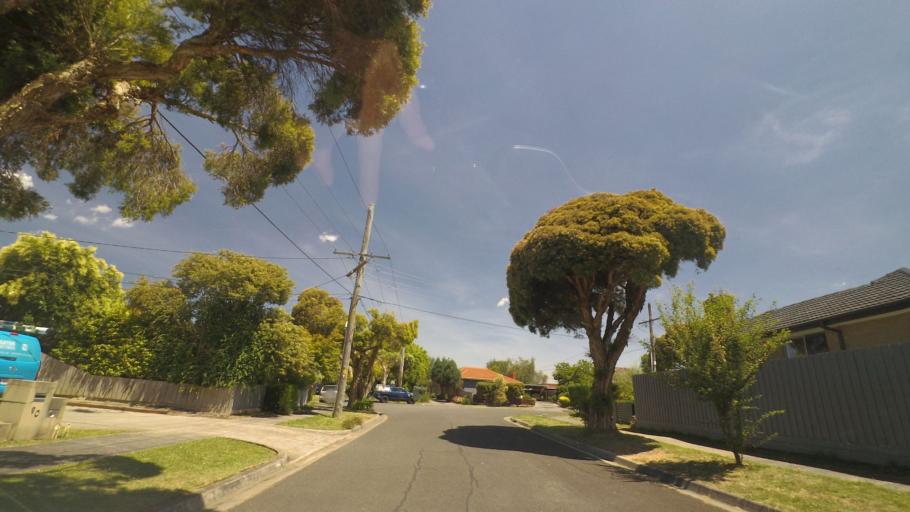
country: AU
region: Victoria
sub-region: Maroondah
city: Bayswater North
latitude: -37.8123
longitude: 145.2969
